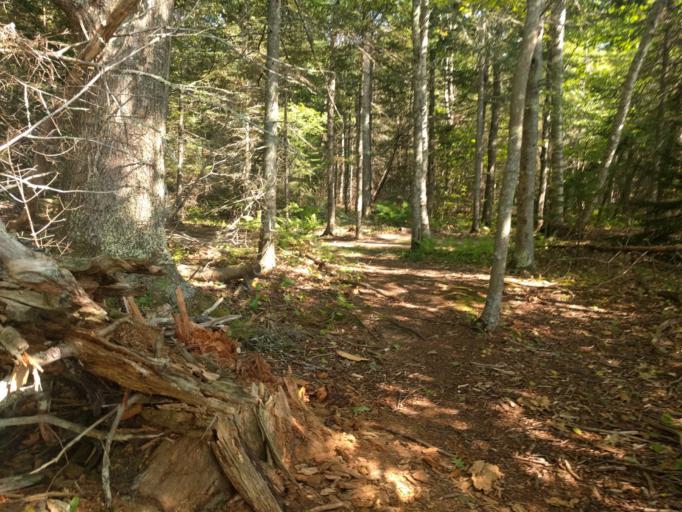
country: US
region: Maine
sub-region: Waldo County
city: Belfast
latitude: 44.4292
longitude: -68.9462
